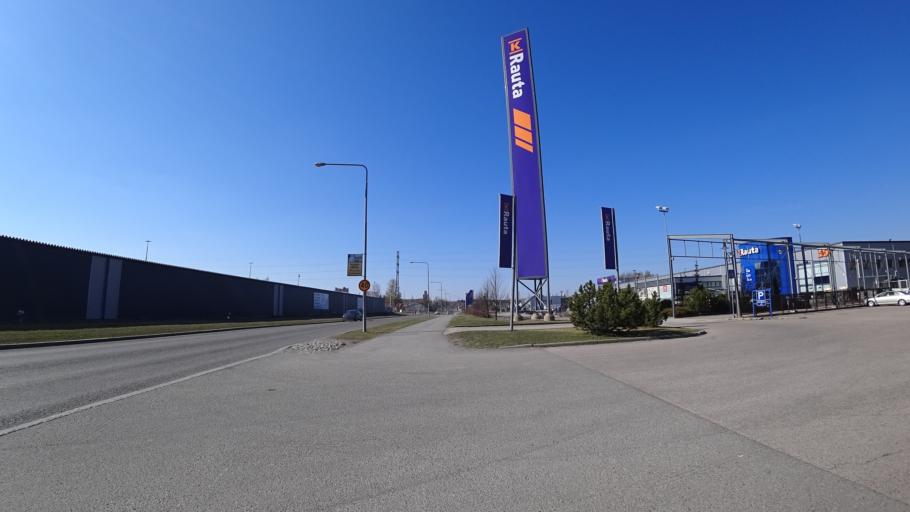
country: FI
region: Pirkanmaa
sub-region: Tampere
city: Pirkkala
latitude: 61.5196
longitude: 23.6582
